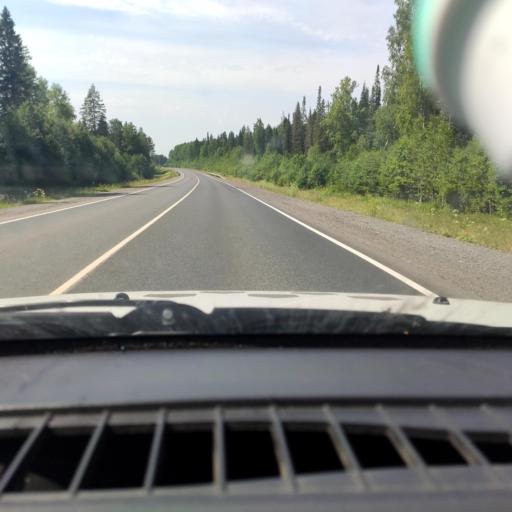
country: RU
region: Perm
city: Zyukayka
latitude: 58.3818
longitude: 54.6103
